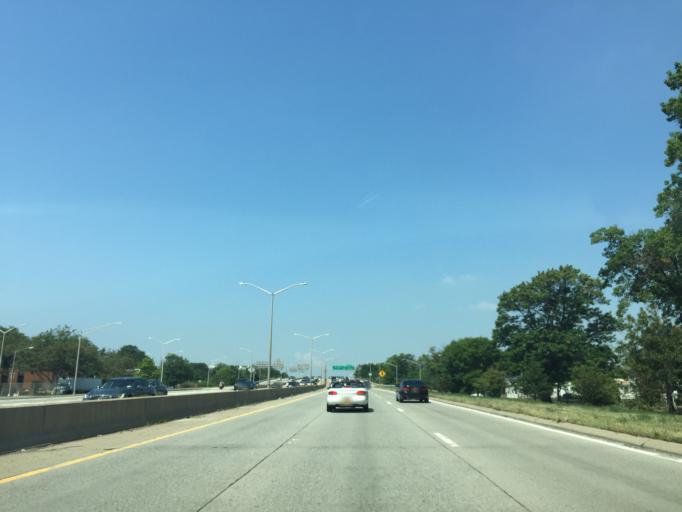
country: US
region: New York
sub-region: Queens County
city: Jamaica
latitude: 40.6676
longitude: -73.7751
